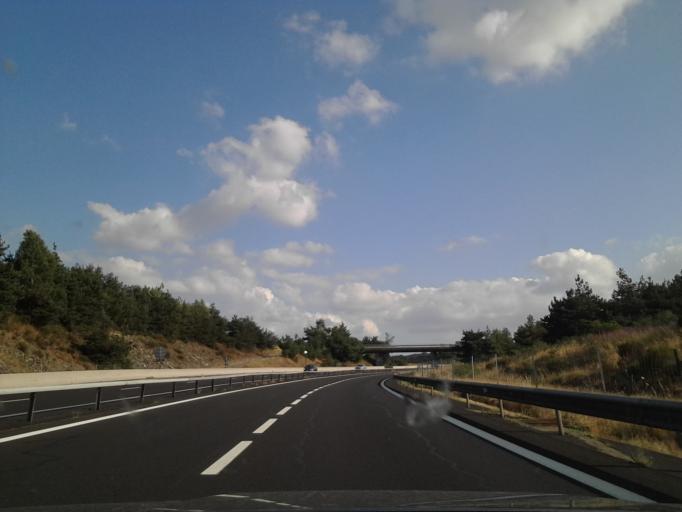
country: FR
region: Auvergne
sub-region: Departement du Cantal
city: Saint-Flour
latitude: 45.1171
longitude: 3.1404
